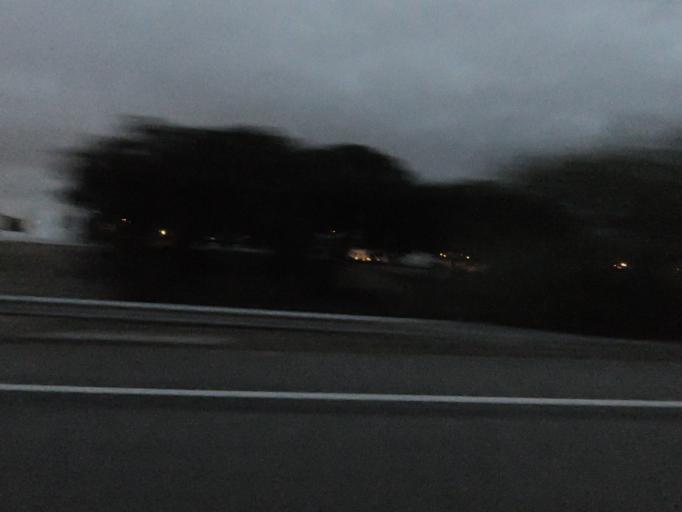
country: PT
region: Setubal
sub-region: Barreiro
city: Santo Antonio da Charneca
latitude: 38.6262
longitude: -9.0366
